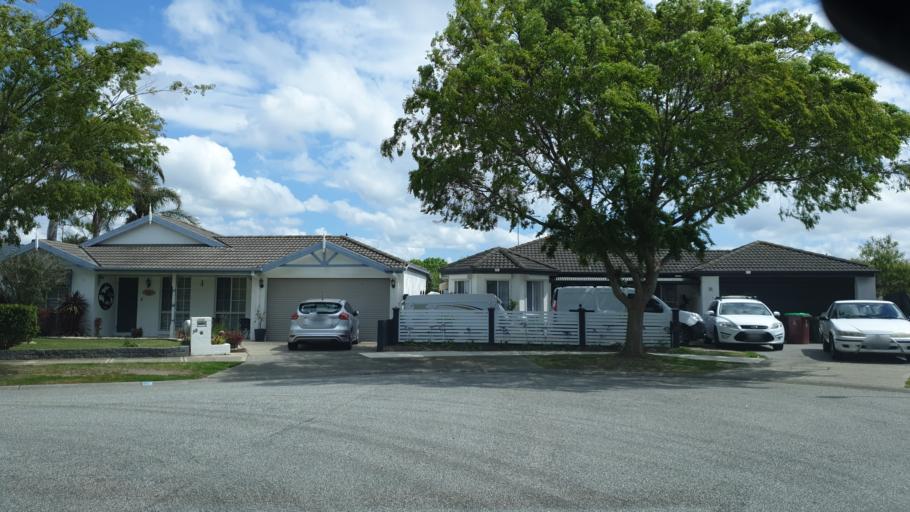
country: AU
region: Victoria
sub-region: Casey
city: Cranbourne North
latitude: -38.0770
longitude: 145.2932
